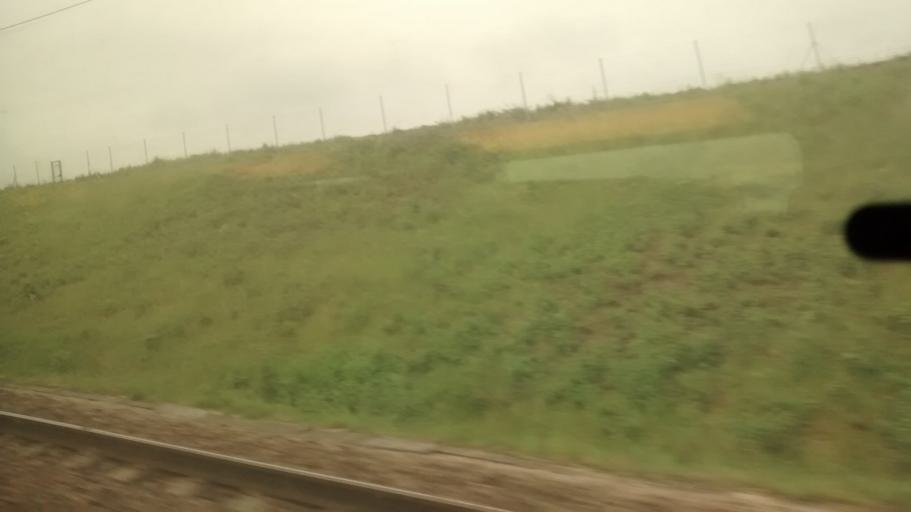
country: FR
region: Ile-de-France
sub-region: Departement de Seine-et-Marne
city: Moisenay
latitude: 48.5580
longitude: 2.7671
